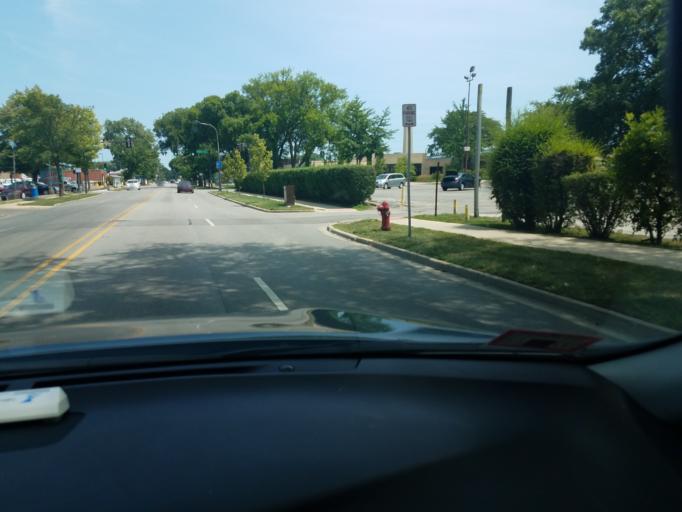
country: US
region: Illinois
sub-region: Cook County
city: Evanston
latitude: 42.0410
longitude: -87.7040
